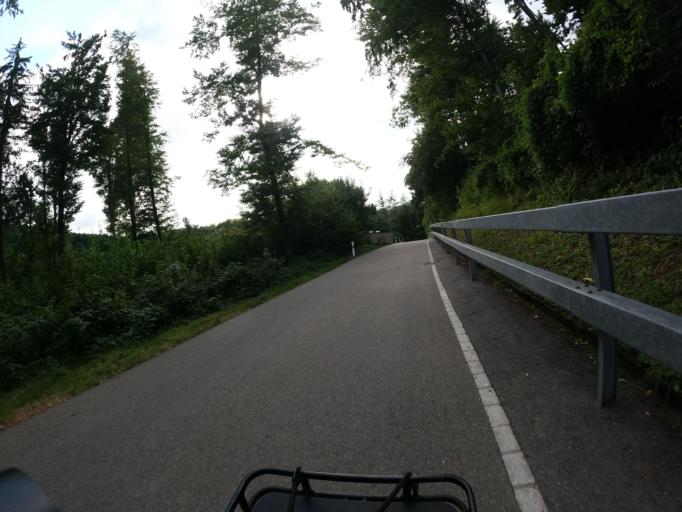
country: CH
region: Aargau
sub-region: Bezirk Bremgarten
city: Rudolfstetten
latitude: 47.3753
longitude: 8.3994
